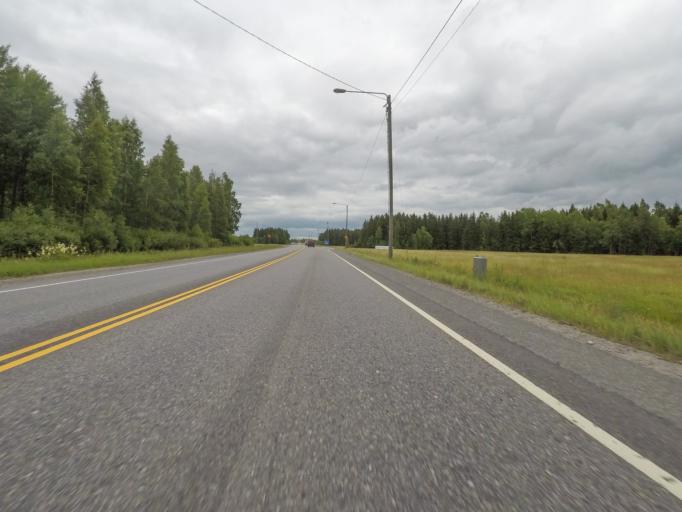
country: FI
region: Varsinais-Suomi
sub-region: Turku
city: Kaarina
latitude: 60.4655
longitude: 22.3940
